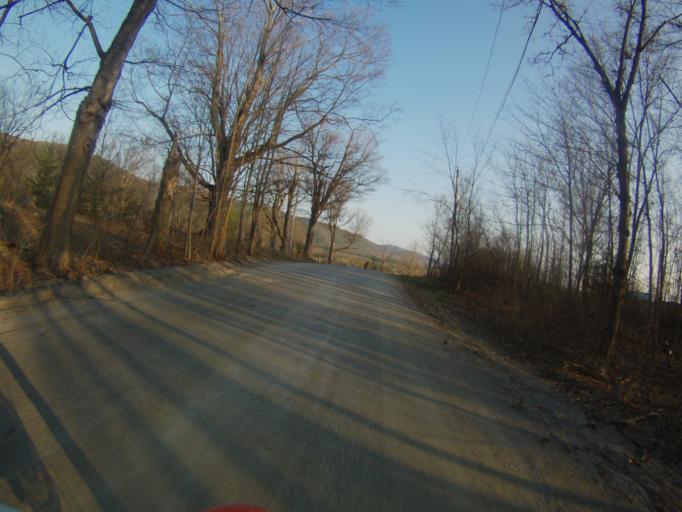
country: US
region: Vermont
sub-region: Addison County
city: Middlebury (village)
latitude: 44.0446
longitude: -73.1039
